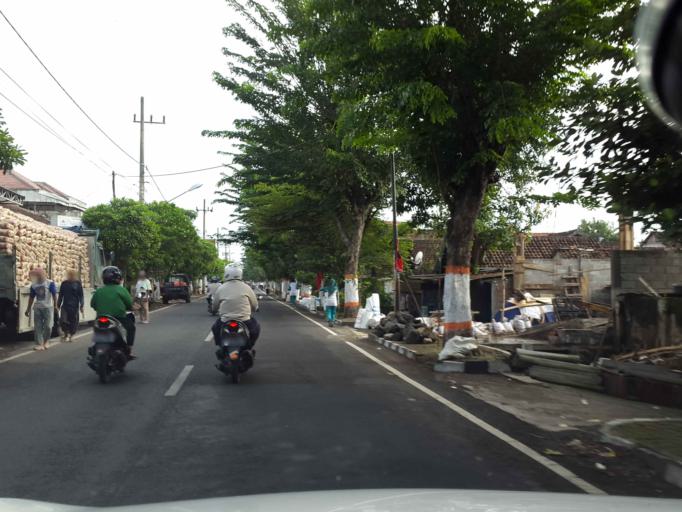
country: ID
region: East Java
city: Mojokerto
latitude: -7.4708
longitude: 112.4295
